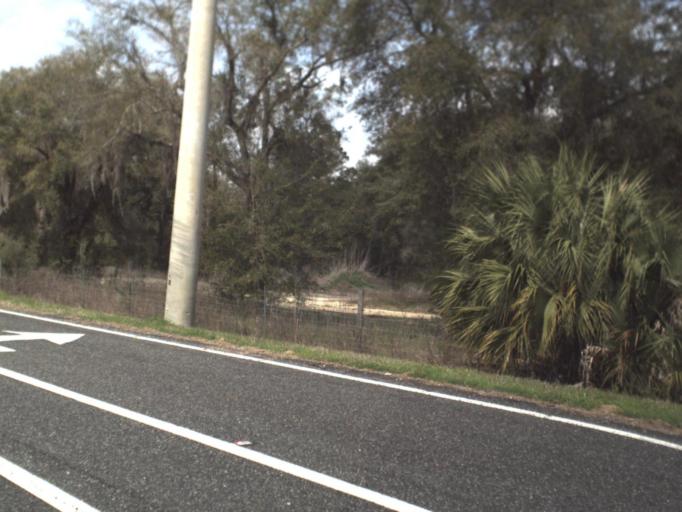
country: US
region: Florida
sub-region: Leon County
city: Woodville
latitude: 30.4133
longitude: -84.0766
